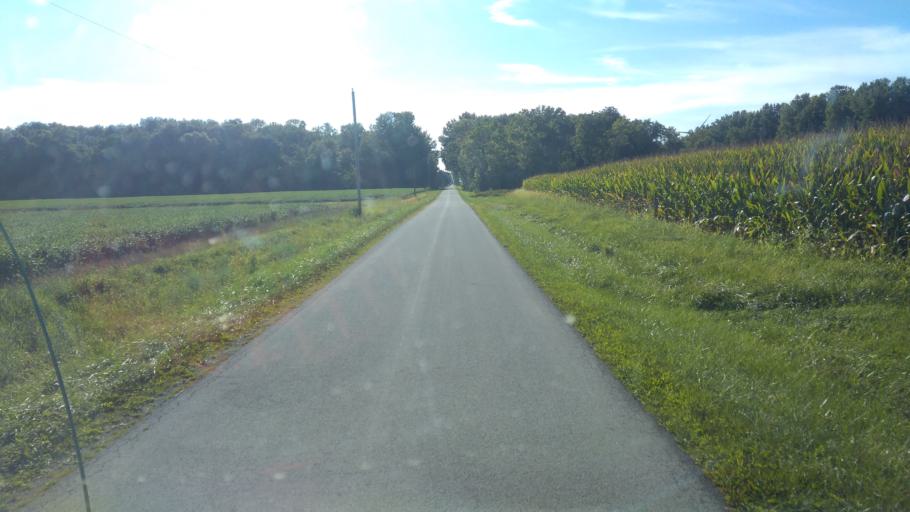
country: US
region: Ohio
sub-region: Hardin County
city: Ada
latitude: 40.7616
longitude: -83.6954
